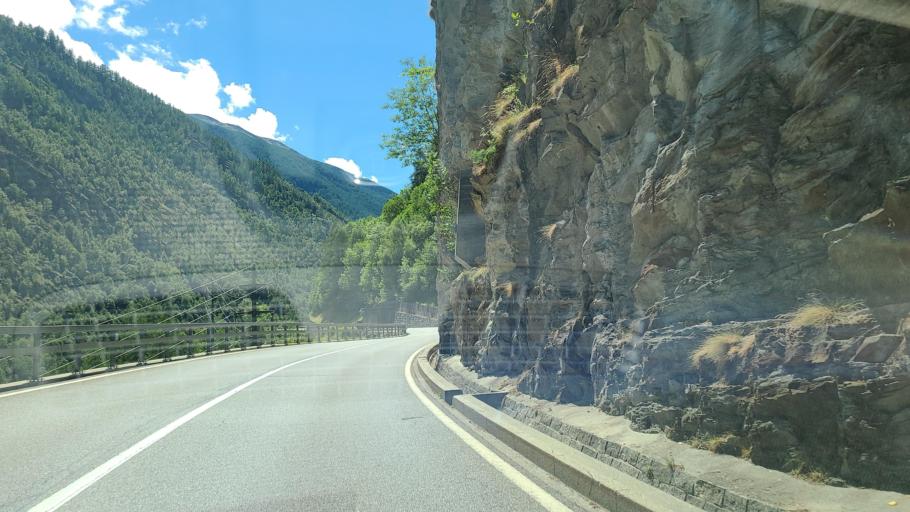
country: CH
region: Valais
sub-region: Visp District
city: Stalden
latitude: 46.2148
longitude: 7.8817
